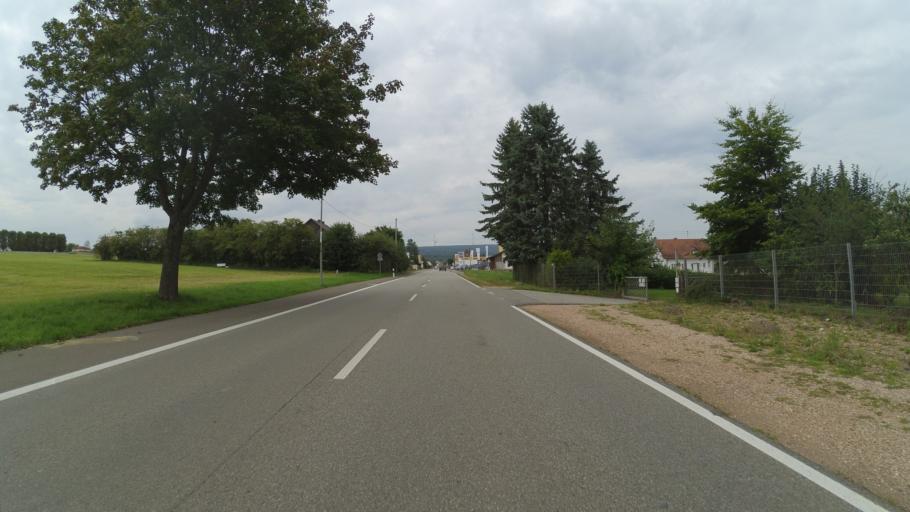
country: DE
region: Saarland
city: Weiskirchen
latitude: 49.5499
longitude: 6.8281
